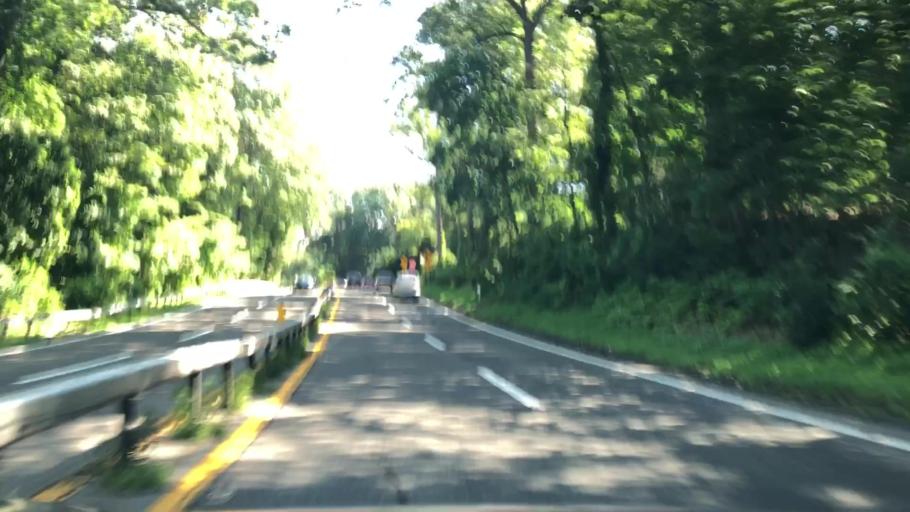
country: US
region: New York
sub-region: Westchester County
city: Hartsdale
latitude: 41.0191
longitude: -73.7873
